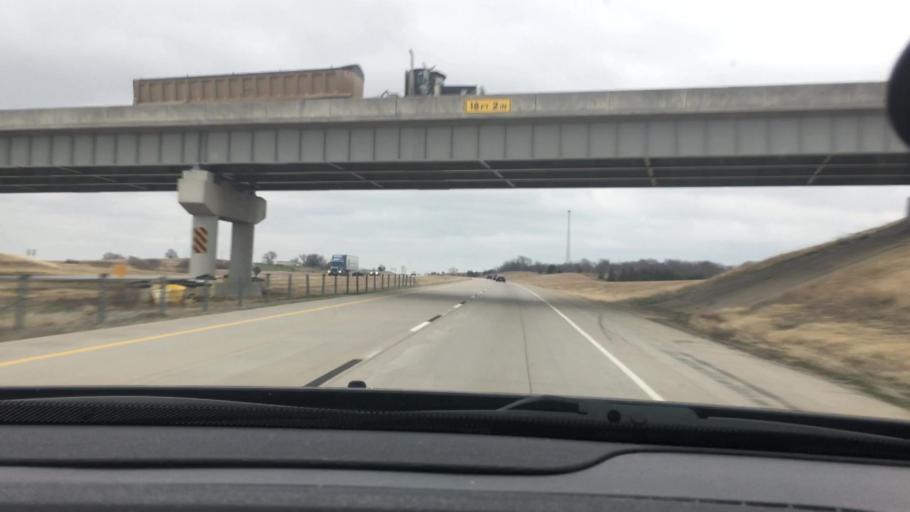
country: US
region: Oklahoma
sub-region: Bryan County
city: Durant
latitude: 34.1317
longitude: -96.2744
